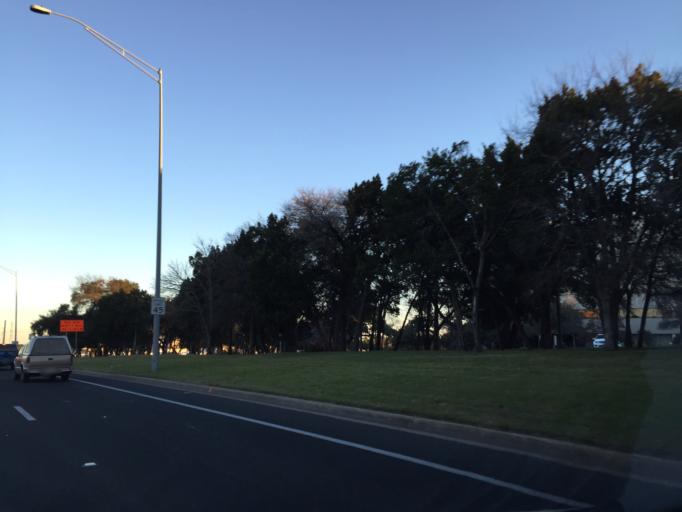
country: US
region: Texas
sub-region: Williamson County
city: Jollyville
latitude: 30.3968
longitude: -97.7350
